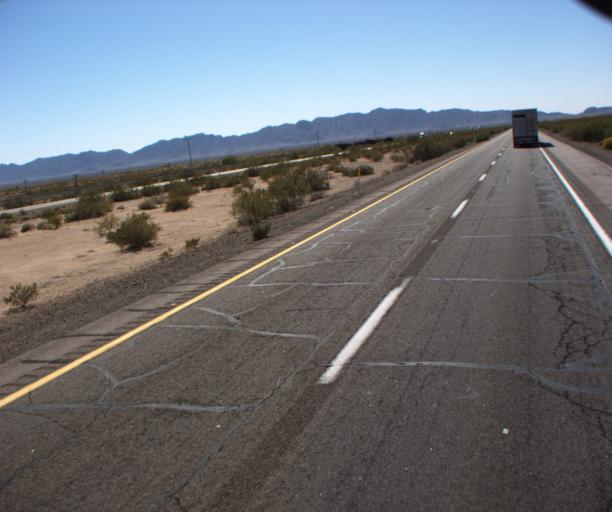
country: US
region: Arizona
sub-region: Yuma County
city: Wellton
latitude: 32.7637
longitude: -113.6284
